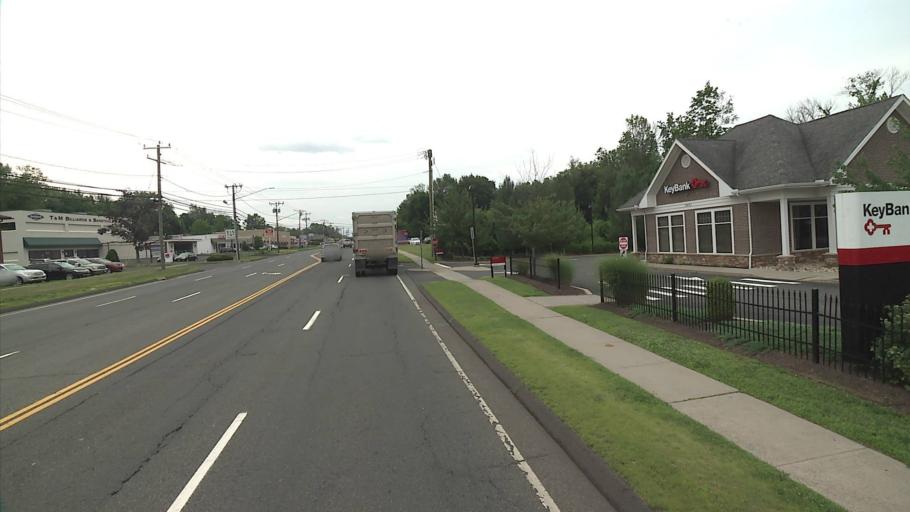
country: US
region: Connecticut
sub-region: Hartford County
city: Wethersfield
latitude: 41.6754
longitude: -72.6489
